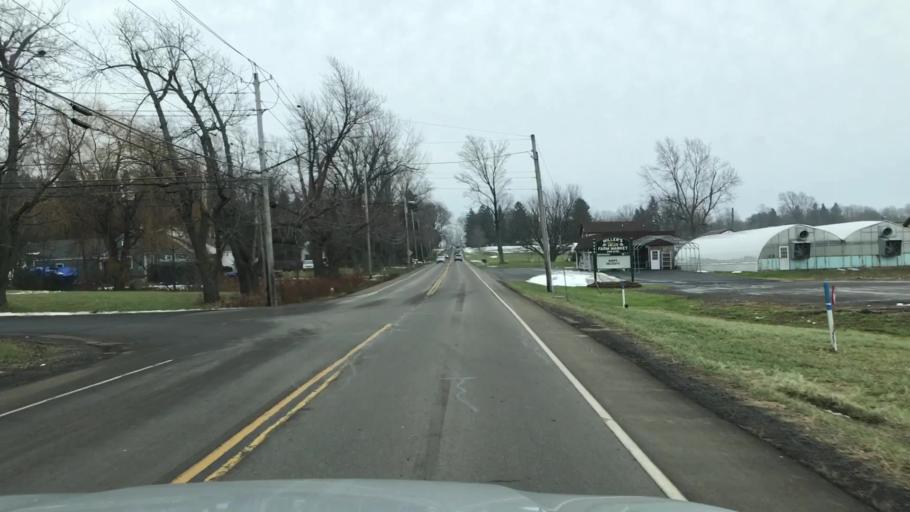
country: US
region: New York
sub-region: Erie County
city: Hamburg
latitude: 42.7449
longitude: -78.8041
